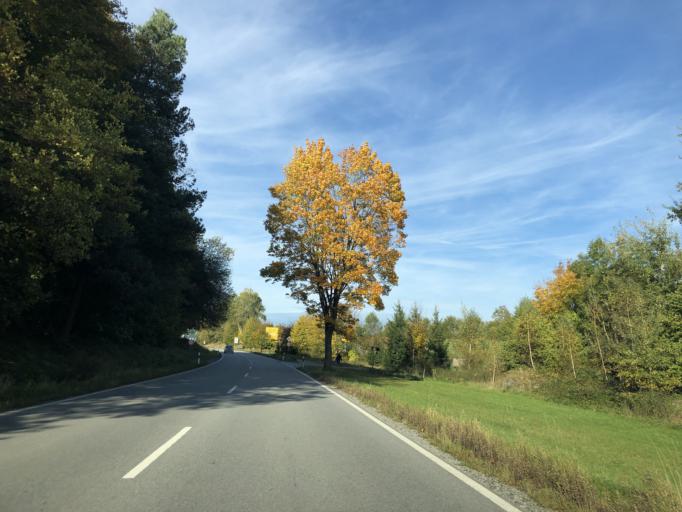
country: DE
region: Bavaria
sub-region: Lower Bavaria
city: Ruhmannsfelden
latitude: 48.9743
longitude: 12.9794
